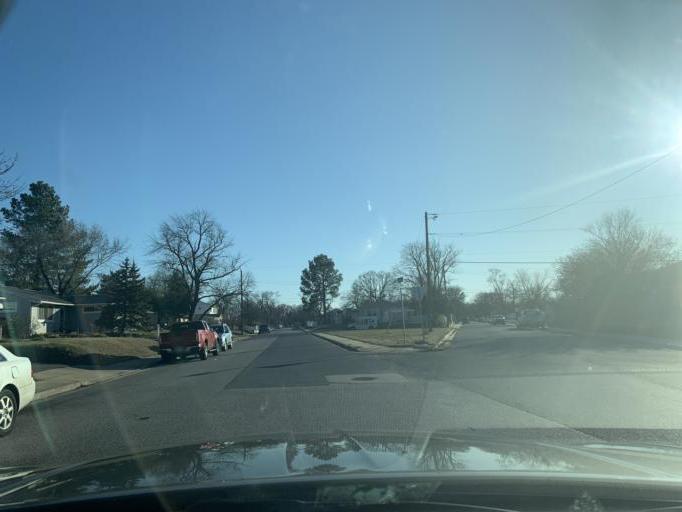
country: US
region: Maryland
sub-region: Anne Arundel County
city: Glen Burnie
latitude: 39.1557
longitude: -76.6253
